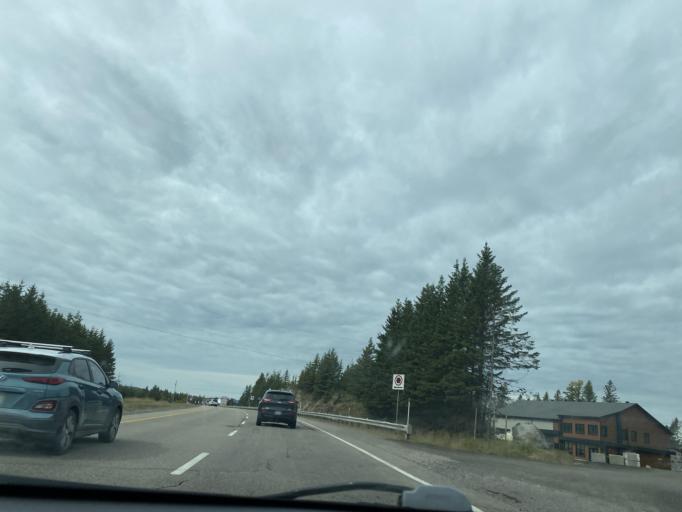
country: CA
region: Quebec
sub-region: Laurentides
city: Mont-Tremblant
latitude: 46.1109
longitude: -74.4954
